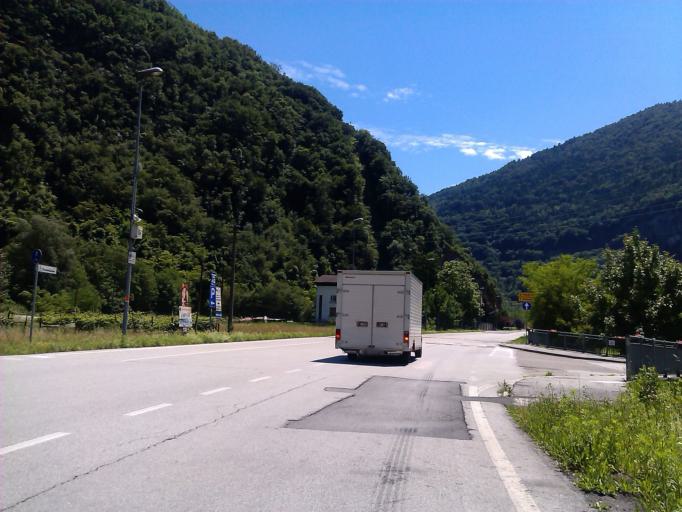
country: IT
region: Veneto
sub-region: Provincia di Vicenza
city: Enego
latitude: 45.9634
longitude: 11.7084
